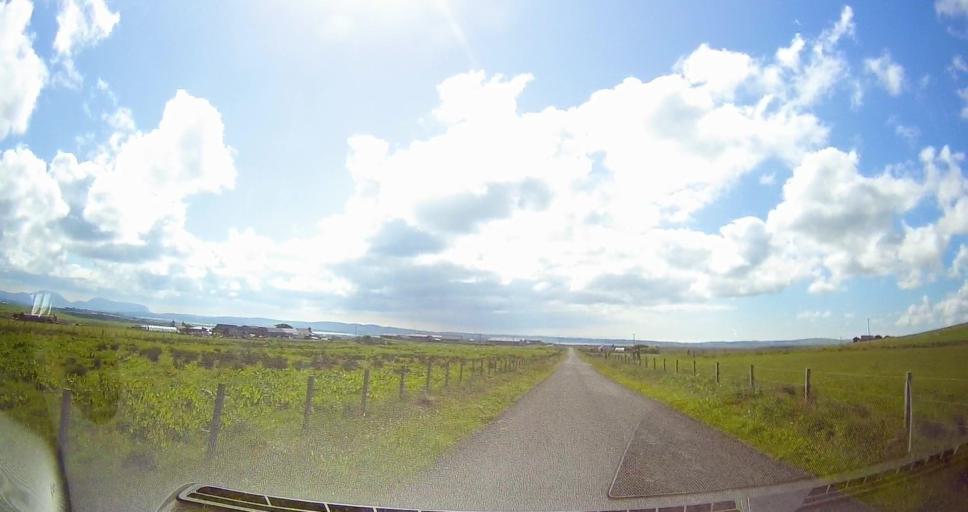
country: GB
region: Scotland
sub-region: Orkney Islands
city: Stromness
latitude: 59.0468
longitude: -3.1446
